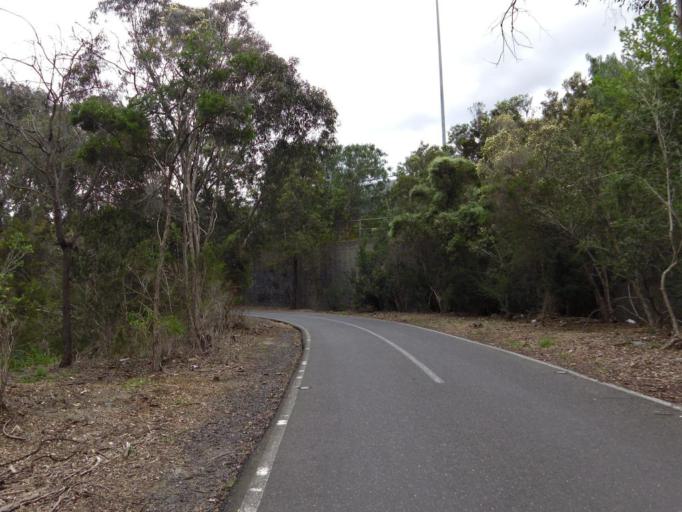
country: AU
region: Victoria
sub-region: Stonnington
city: Glen Iris
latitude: -37.8517
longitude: 145.0533
